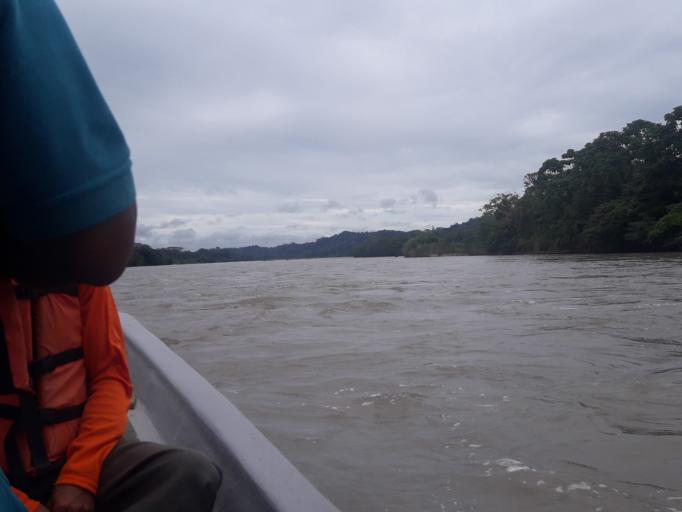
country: EC
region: Orellana
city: Boca Suno
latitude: -0.8819
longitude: -77.2986
